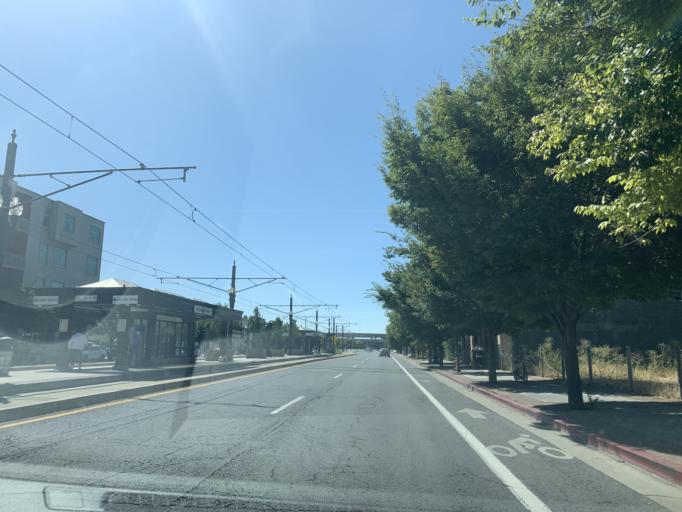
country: US
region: Utah
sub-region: Salt Lake County
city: Salt Lake City
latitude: 40.7651
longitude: -111.9057
